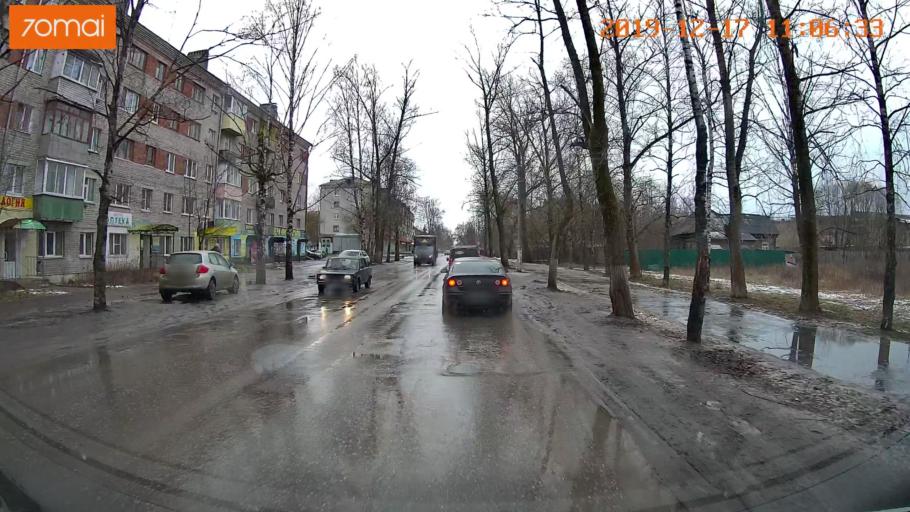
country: RU
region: Vladimir
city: Gus'-Khrustal'nyy
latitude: 55.6151
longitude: 40.6446
